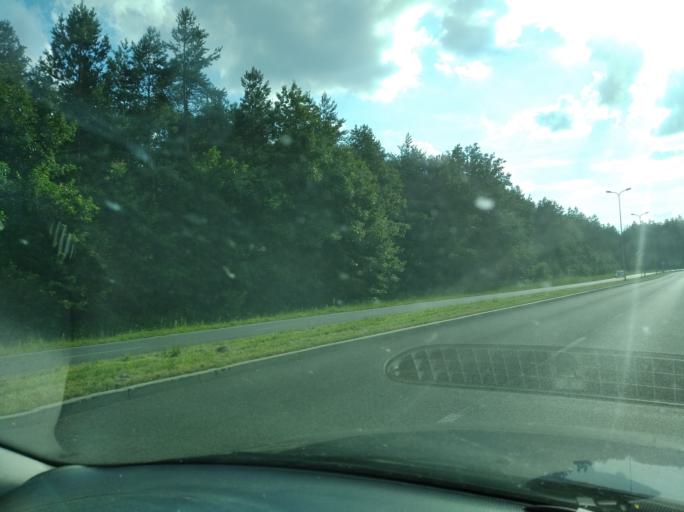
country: PL
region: Subcarpathian Voivodeship
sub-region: Powiat rzeszowski
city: Rudna Mala
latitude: 50.1139
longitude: 21.9893
